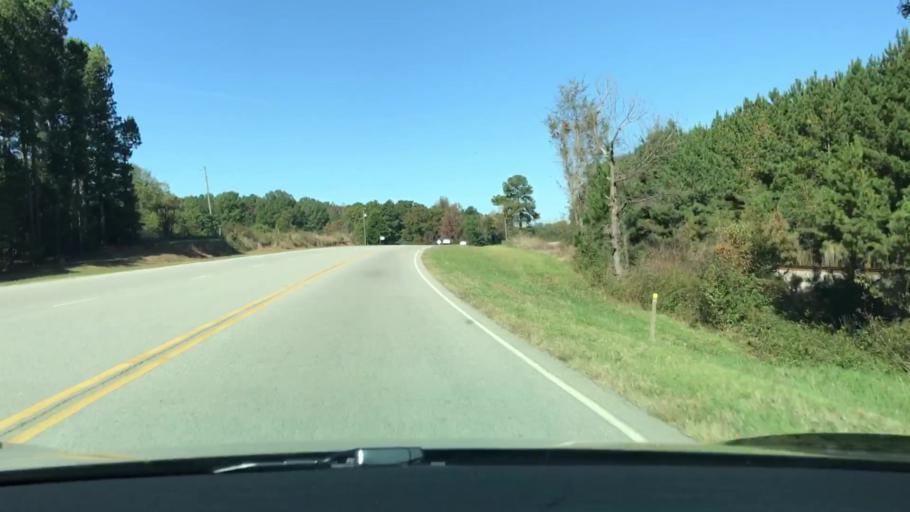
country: US
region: Georgia
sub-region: Warren County
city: Firing Range
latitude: 33.4858
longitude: -82.7943
